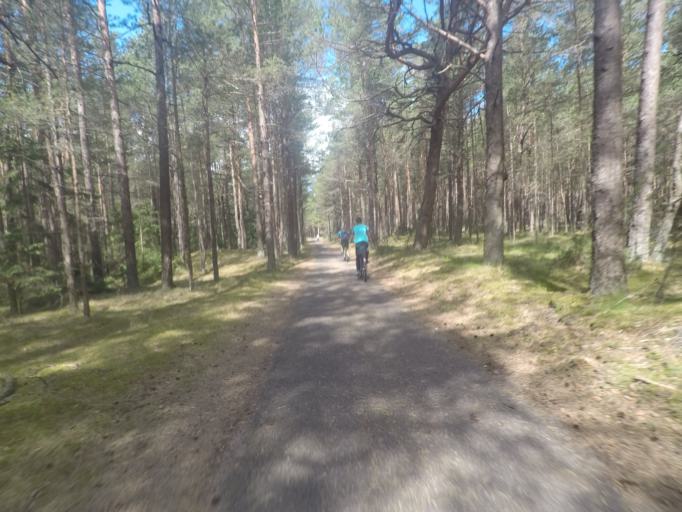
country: LT
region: Klaipedos apskritis
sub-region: Klaipeda
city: Klaipeda
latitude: 55.5585
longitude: 21.1069
